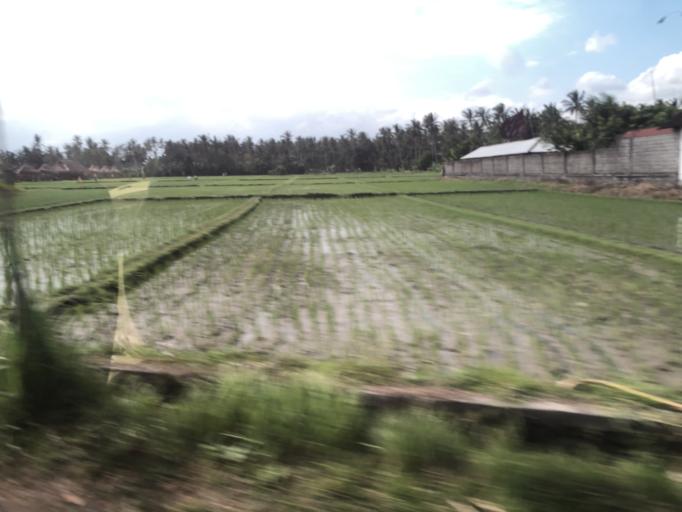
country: ID
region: Bali
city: Banjar Bucu
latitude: -8.5769
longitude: 115.1997
